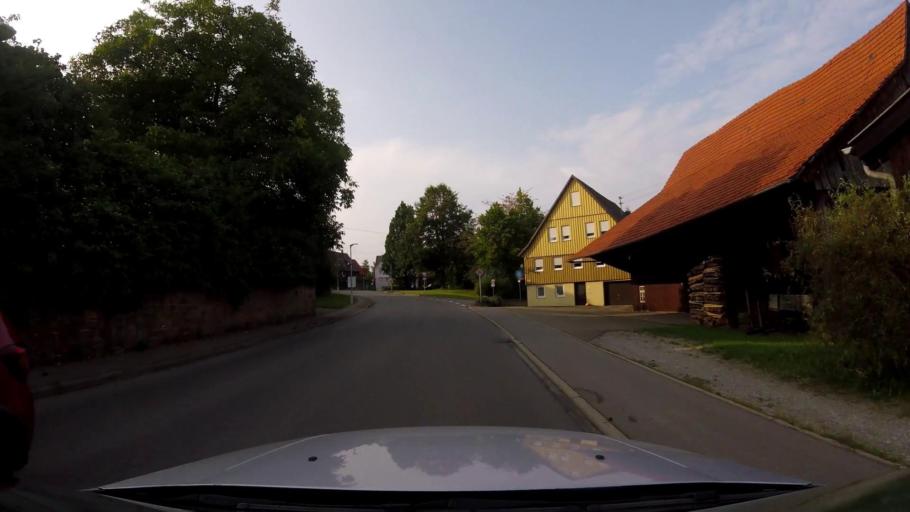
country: DE
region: Baden-Wuerttemberg
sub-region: Regierungsbezirk Stuttgart
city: Welzheim
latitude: 48.8563
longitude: 9.6257
